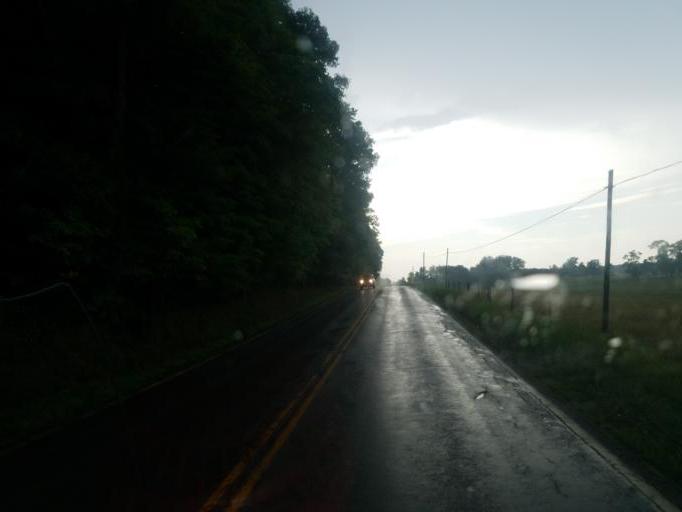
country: US
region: Ohio
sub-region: Wayne County
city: Creston
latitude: 40.9457
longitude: -81.8846
